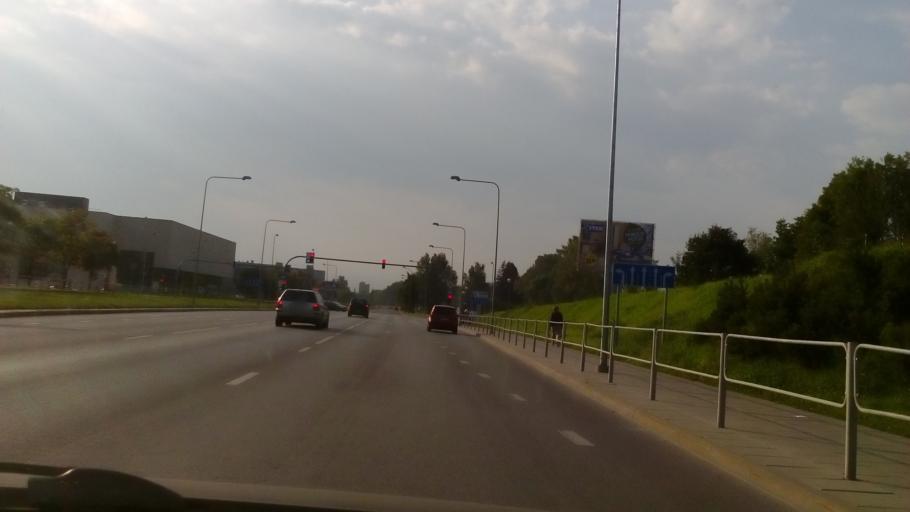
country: LT
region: Alytaus apskritis
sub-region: Alytus
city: Alytus
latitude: 54.4056
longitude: 24.0192
